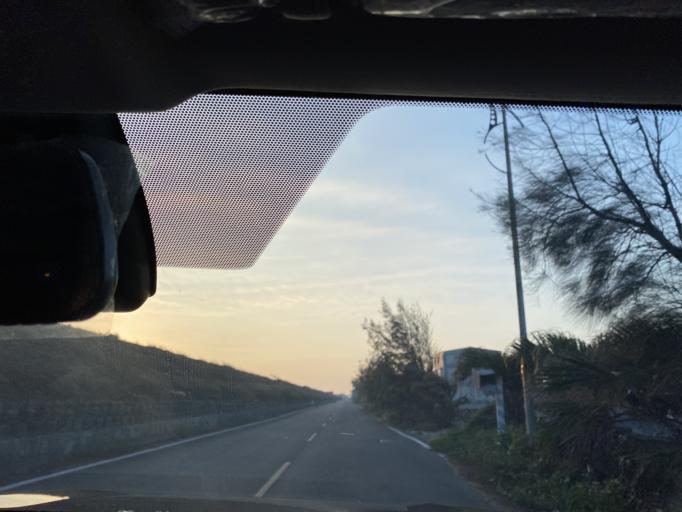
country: TW
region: Taiwan
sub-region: Changhua
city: Chang-hua
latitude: 23.9682
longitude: 120.3332
